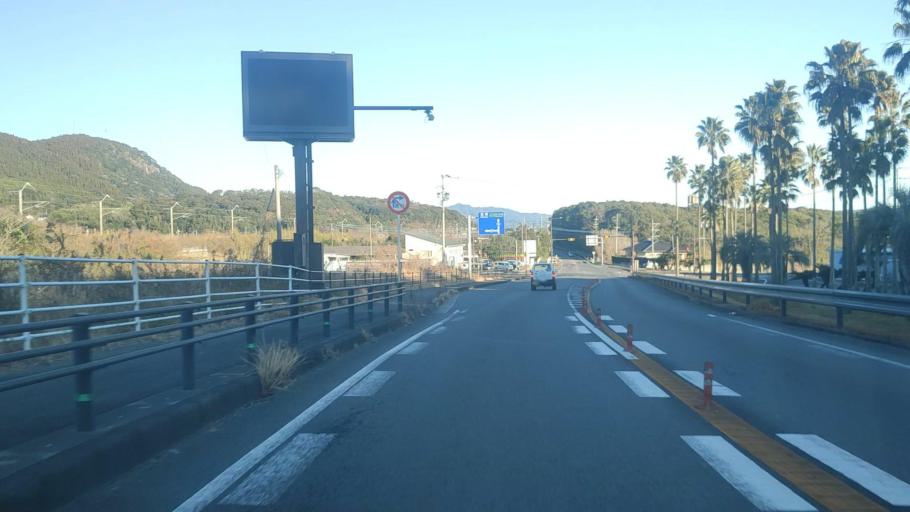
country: JP
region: Miyazaki
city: Nobeoka
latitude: 32.3783
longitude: 131.6276
